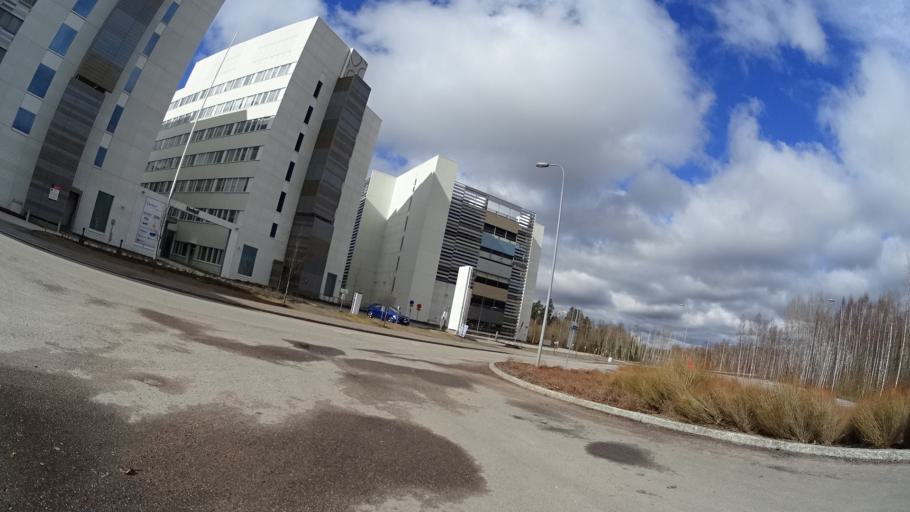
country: FI
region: Uusimaa
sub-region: Helsinki
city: Teekkarikylae
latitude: 60.2092
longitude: 24.8360
